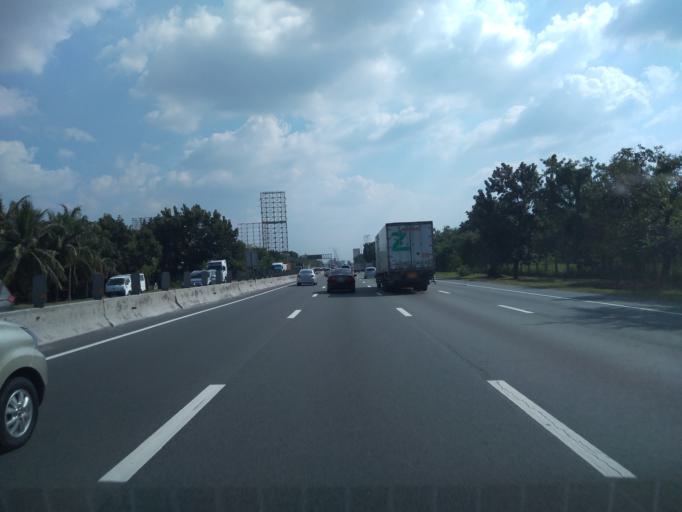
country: PH
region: Calabarzon
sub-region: Province of Laguna
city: San Pedro
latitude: 14.3731
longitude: 121.0429
